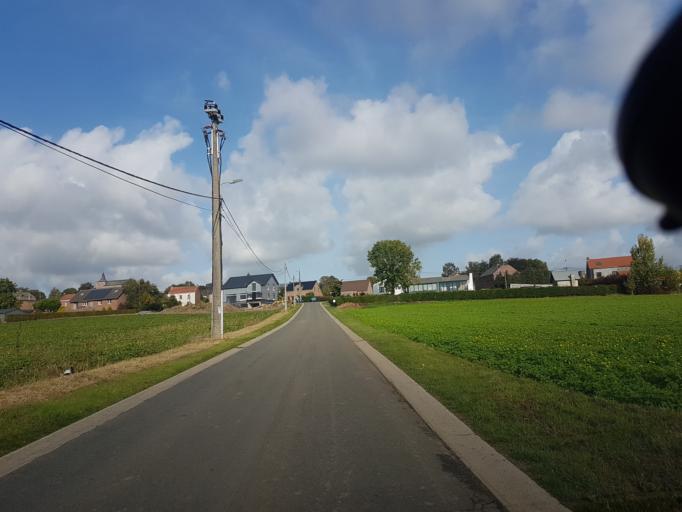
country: BE
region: Wallonia
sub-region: Province de Liege
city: Heron
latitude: 50.5477
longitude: 5.1020
